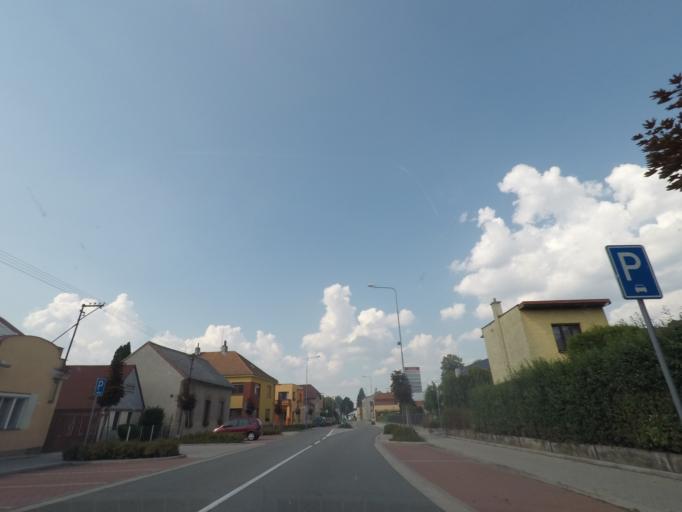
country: CZ
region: Pardubicky
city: Horni Jeleni
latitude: 50.0494
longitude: 16.0841
